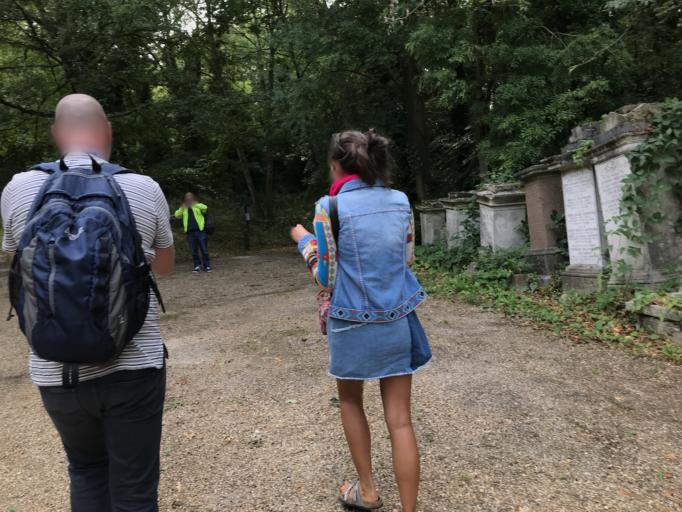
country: GB
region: England
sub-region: Greater London
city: Catford
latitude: 51.4629
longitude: -0.0518
